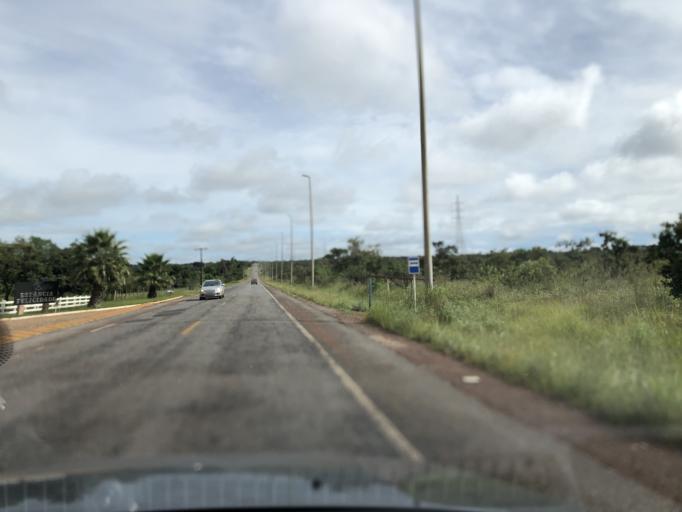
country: BR
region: Federal District
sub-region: Brasilia
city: Brasilia
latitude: -15.7157
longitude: -48.0871
